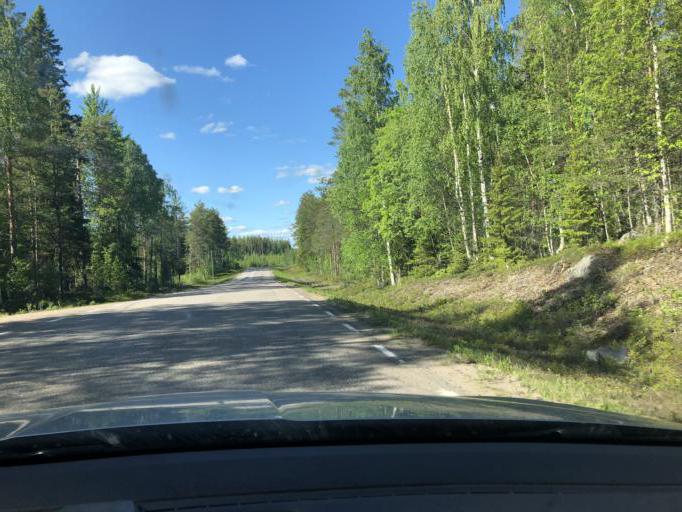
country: SE
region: Norrbotten
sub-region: Kalix Kommun
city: Kalix
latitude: 65.8843
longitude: 23.1521
